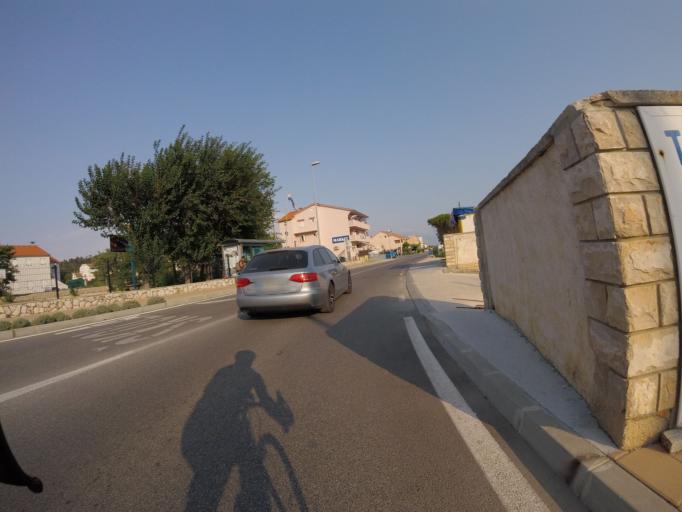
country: HR
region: Primorsko-Goranska
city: Lopar
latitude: 44.8298
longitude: 14.7316
